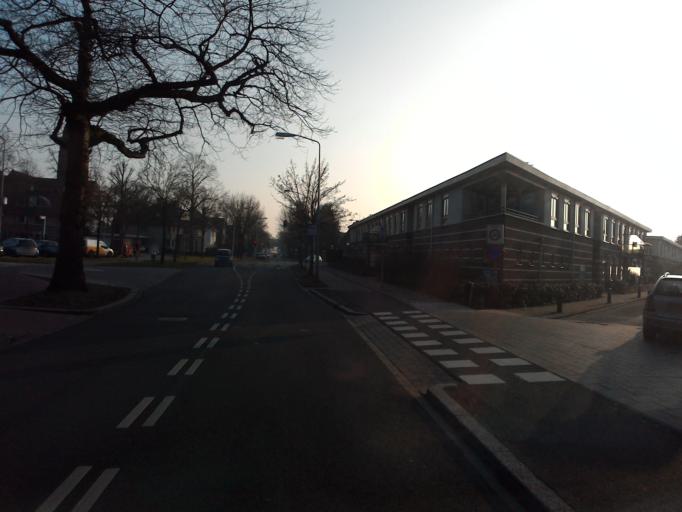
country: NL
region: Utrecht
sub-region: Gemeente Zeist
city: Zeist
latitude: 52.0966
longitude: 5.2439
